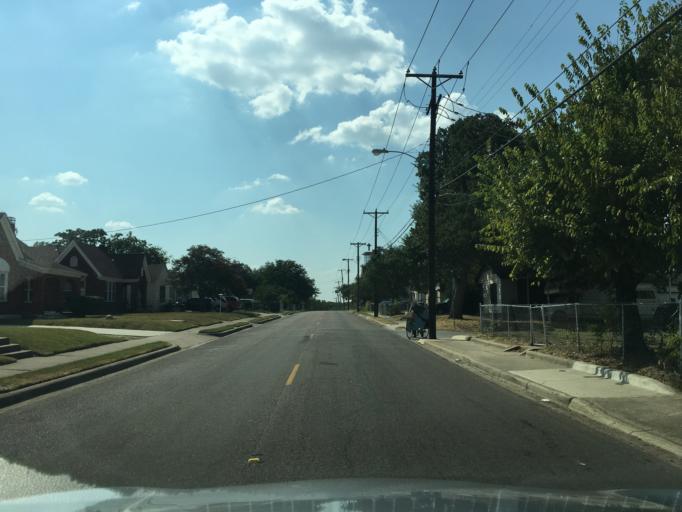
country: US
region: Texas
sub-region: Dallas County
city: Dallas
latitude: 32.7392
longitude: -96.8076
